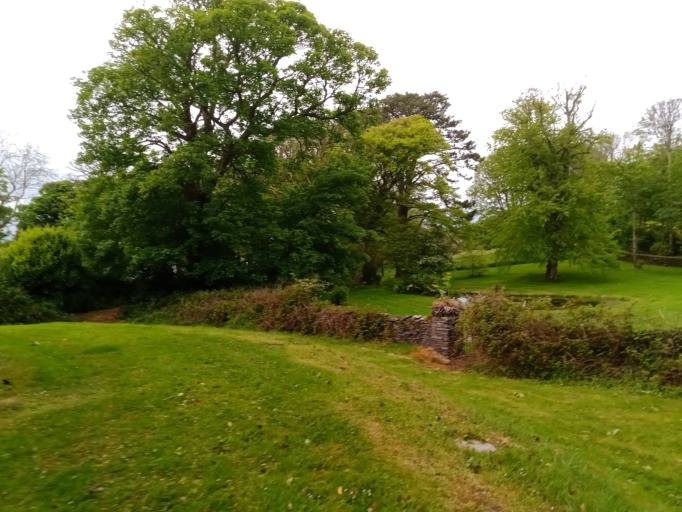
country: IE
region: Munster
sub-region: County Cork
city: Skibbereen
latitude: 51.5224
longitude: -9.3369
